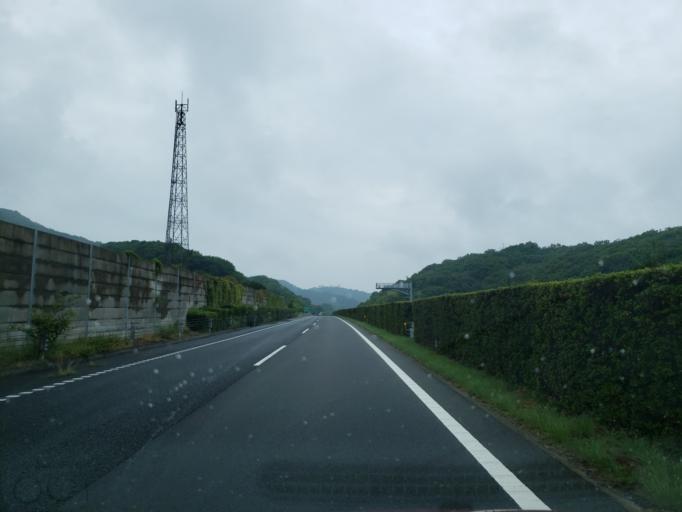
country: JP
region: Hyogo
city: Fukura
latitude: 34.2684
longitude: 134.6933
